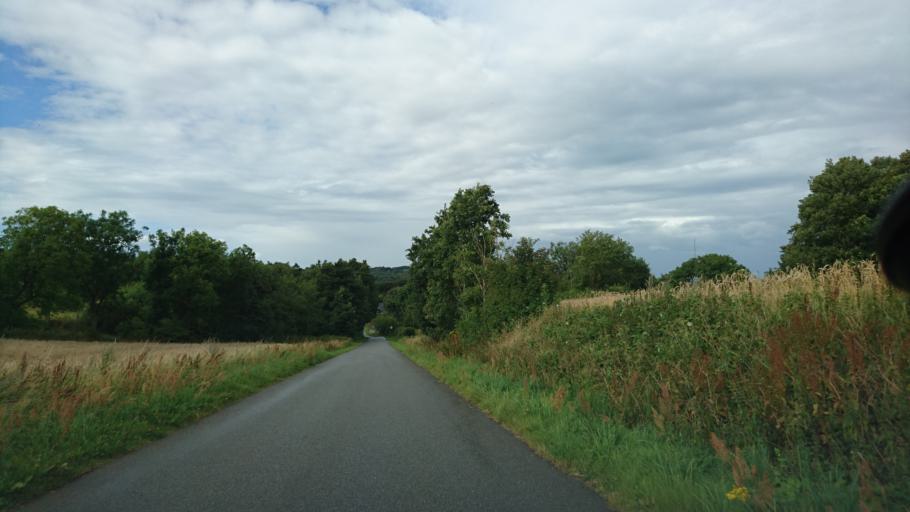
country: DK
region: North Denmark
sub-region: Frederikshavn Kommune
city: Frederikshavn
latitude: 57.3971
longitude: 10.4778
